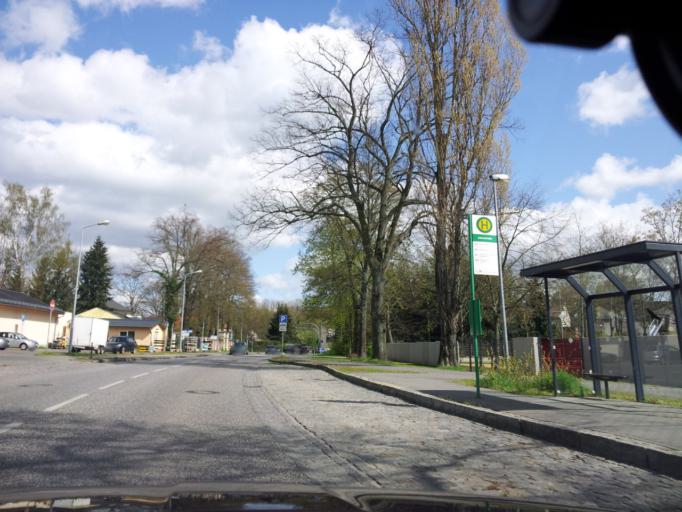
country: DE
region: Brandenburg
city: Bernau bei Berlin
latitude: 52.6820
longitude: 13.5945
